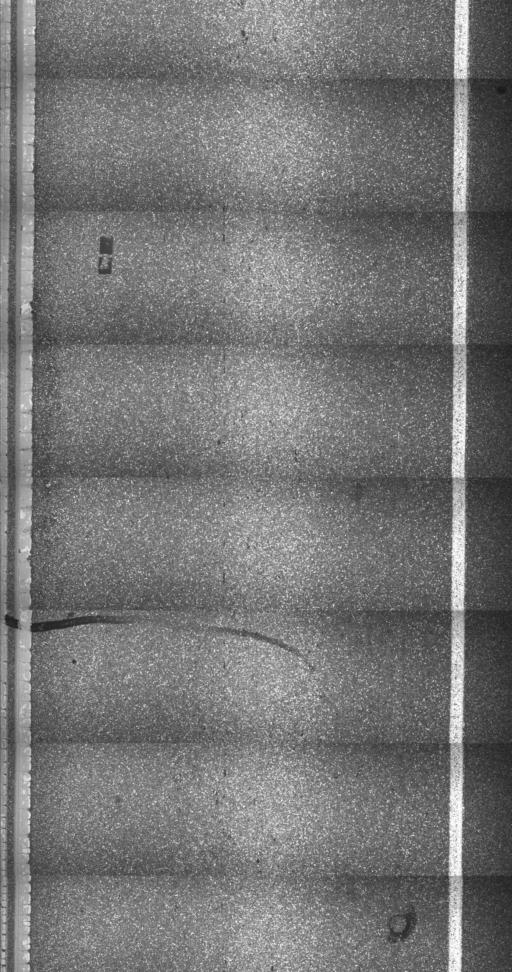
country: US
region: Vermont
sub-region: Windsor County
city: Wilder
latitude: 43.6643
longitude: -72.3145
